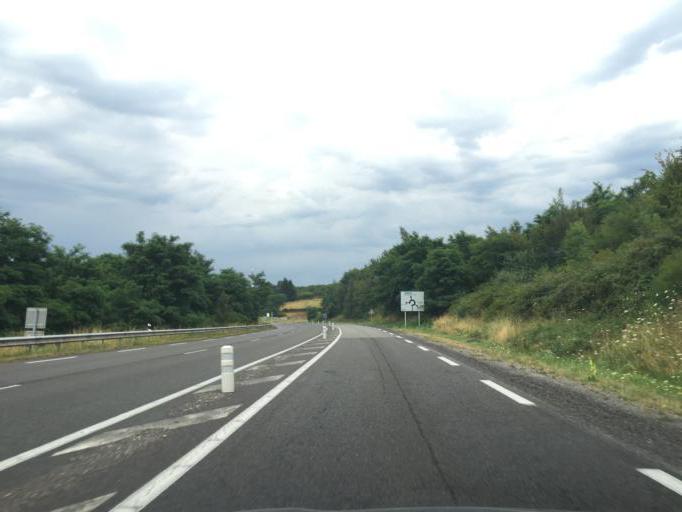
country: FR
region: Rhone-Alpes
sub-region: Departement de la Loire
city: La Pacaudiere
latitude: 46.2059
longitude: 3.8118
